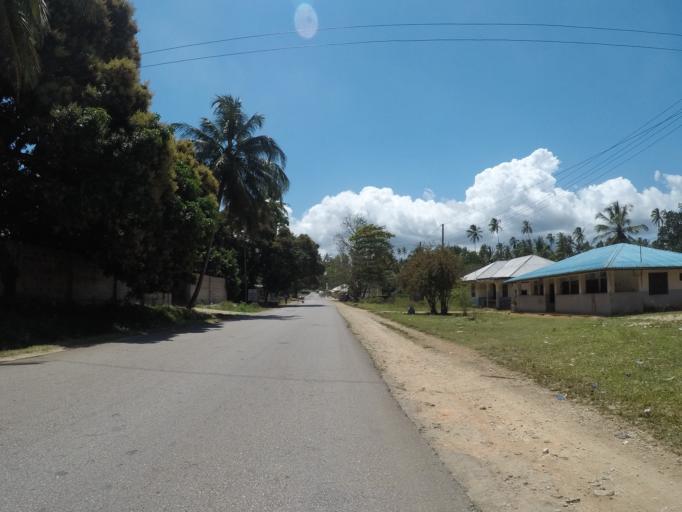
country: TZ
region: Zanzibar Central/South
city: Koani
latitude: -6.2058
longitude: 39.3251
